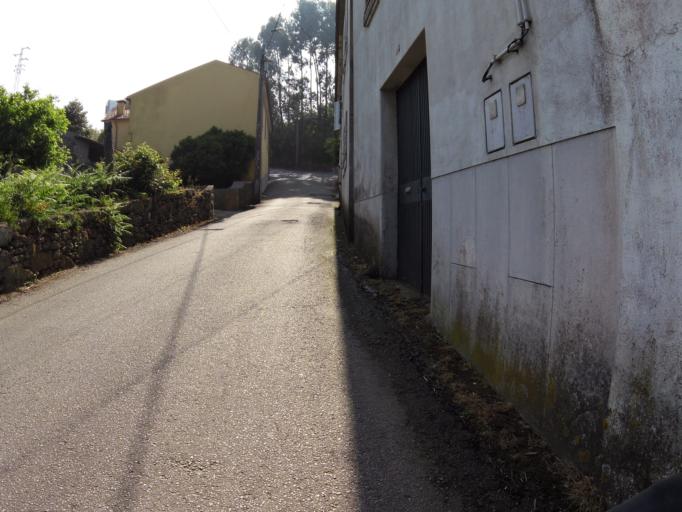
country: PT
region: Porto
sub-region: Vila Nova de Gaia
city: Olival
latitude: 41.0394
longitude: -8.5366
